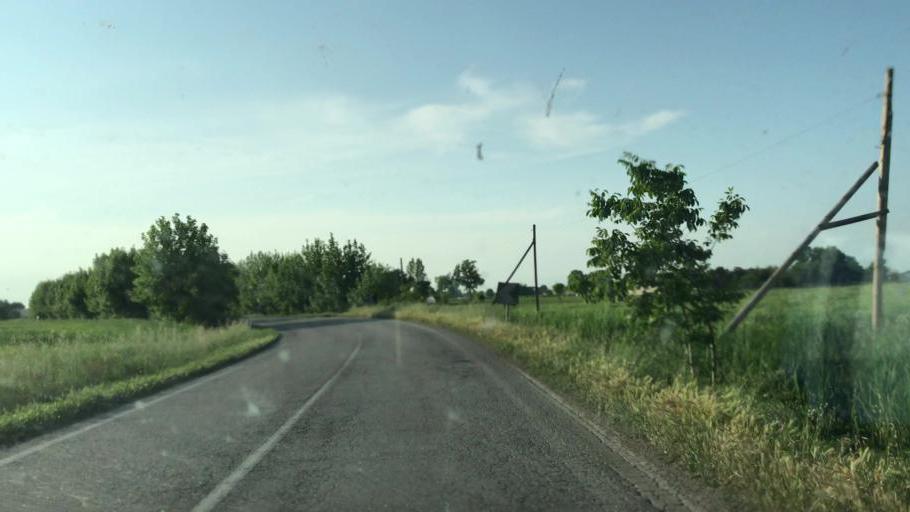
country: IT
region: Lombardy
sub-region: Provincia di Mantova
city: Piubega
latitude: 45.2415
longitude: 10.5064
